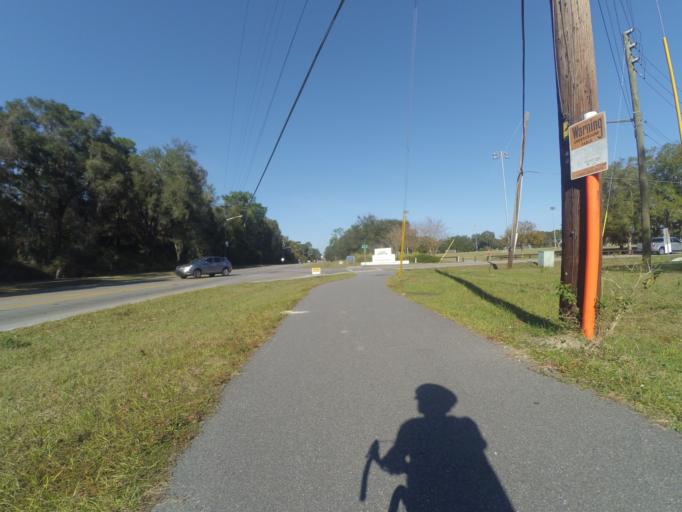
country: US
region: Florida
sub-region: Alachua County
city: Gainesville
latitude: 29.6160
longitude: -82.4224
